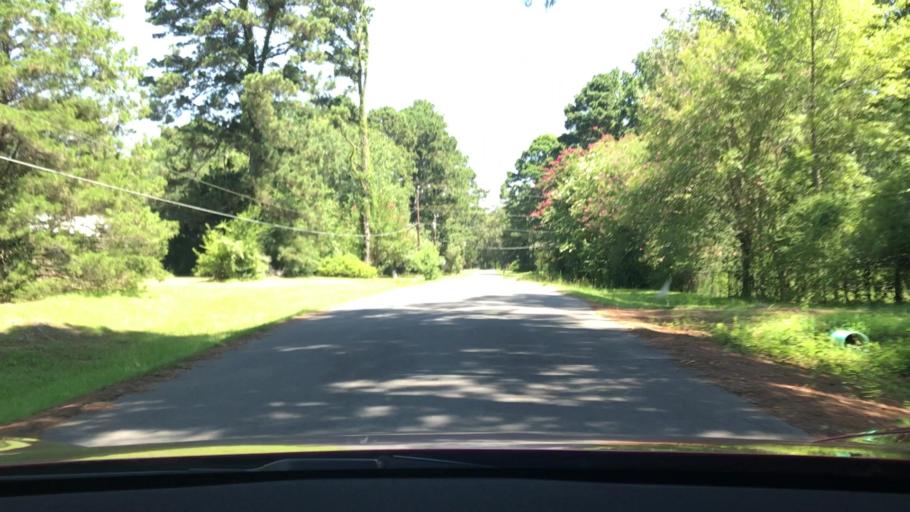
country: US
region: Louisiana
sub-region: De Soto Parish
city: Stonewall
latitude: 32.3440
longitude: -93.7085
